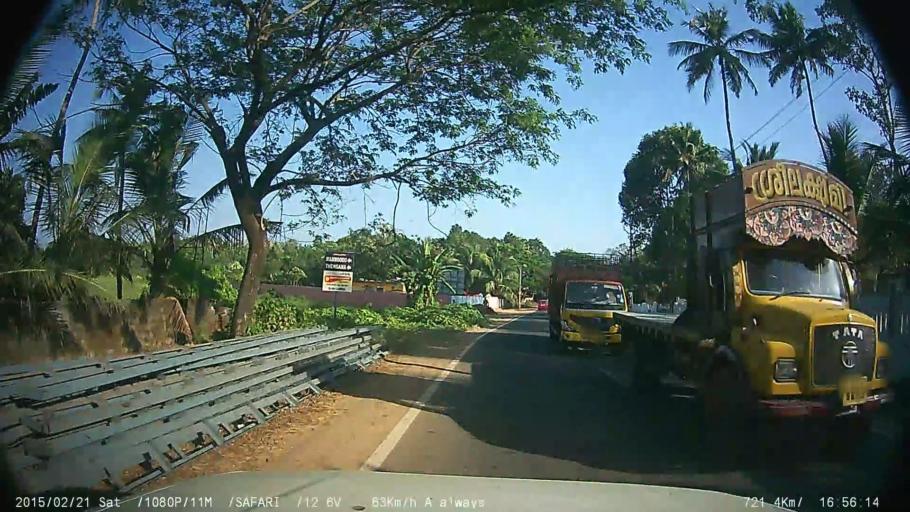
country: IN
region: Kerala
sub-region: Kottayam
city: Changanacheri
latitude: 9.4605
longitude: 76.5364
